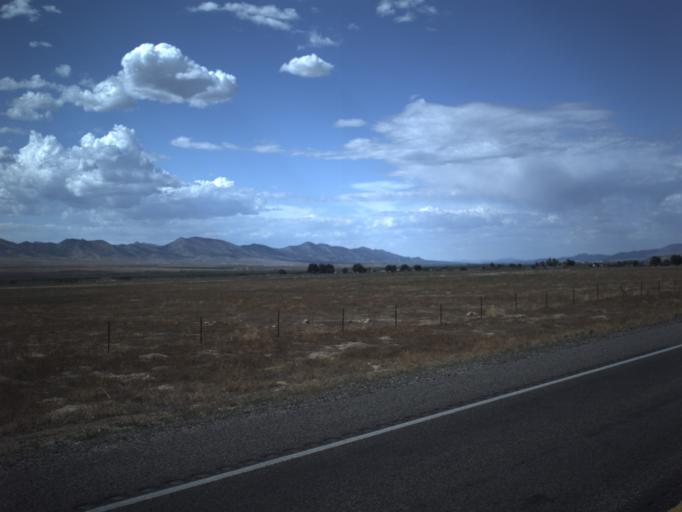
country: US
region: Utah
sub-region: Sevier County
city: Salina
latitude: 39.0301
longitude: -111.8299
